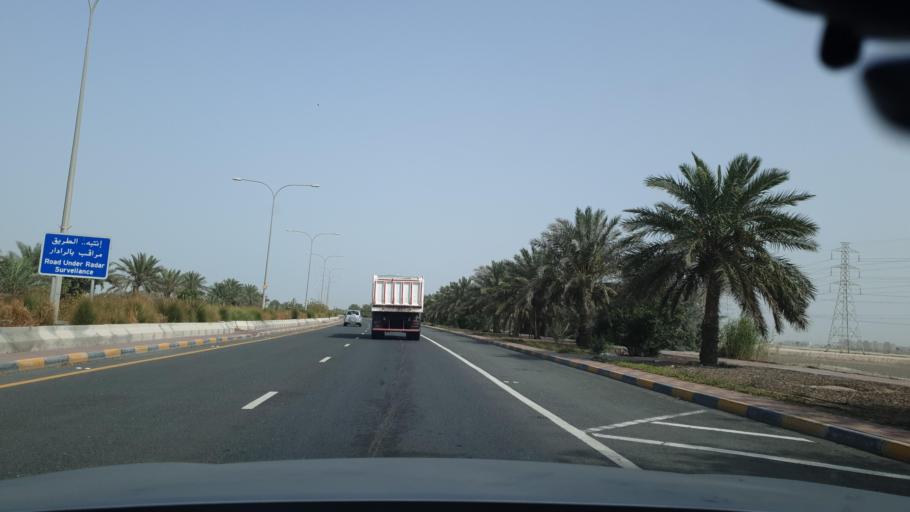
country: QA
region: Al Wakrah
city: Umm Sa'id
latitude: 25.0126
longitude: 51.5545
